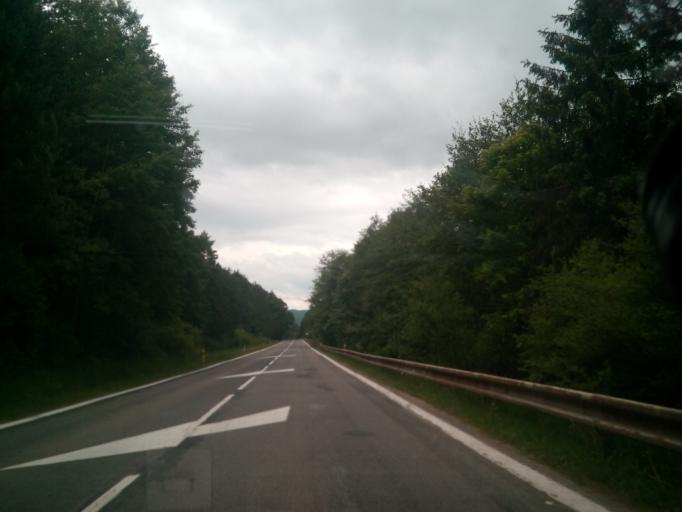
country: SK
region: Kosicky
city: Krompachy
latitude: 48.9973
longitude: 20.8905
